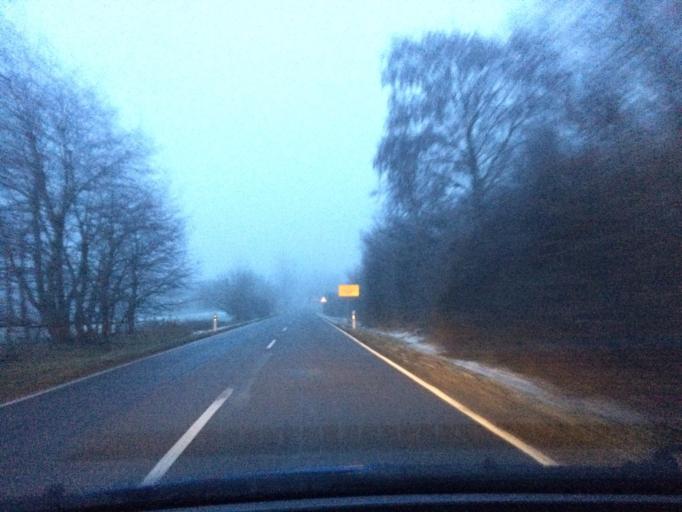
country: DE
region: Schleswig-Holstein
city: Wiershop
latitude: 53.4442
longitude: 10.4491
